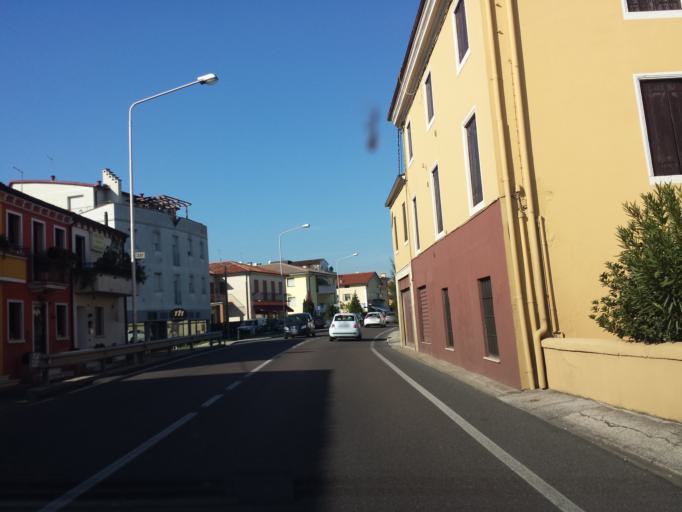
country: IT
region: Veneto
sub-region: Provincia di Vicenza
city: Crispi Cavour
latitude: 45.5741
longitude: 11.5112
